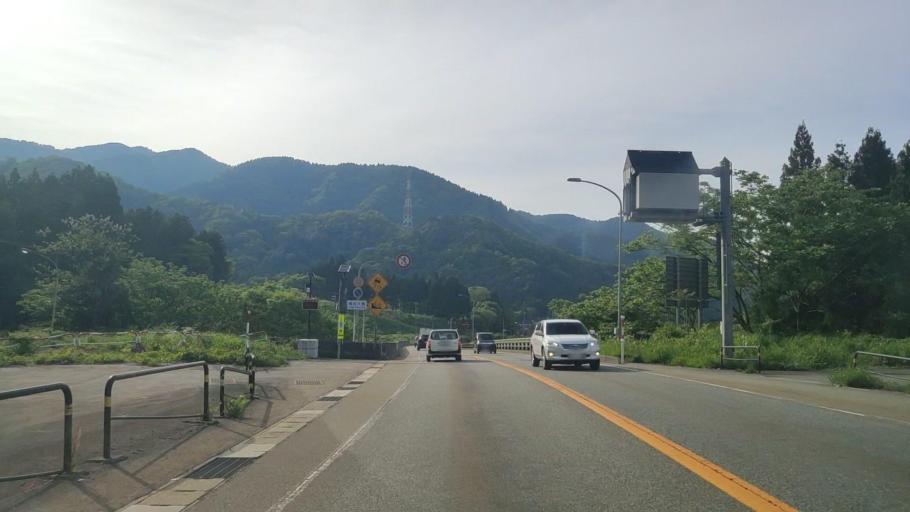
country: JP
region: Toyama
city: Yatsuomachi-higashikumisaka
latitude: 36.5050
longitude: 137.2320
